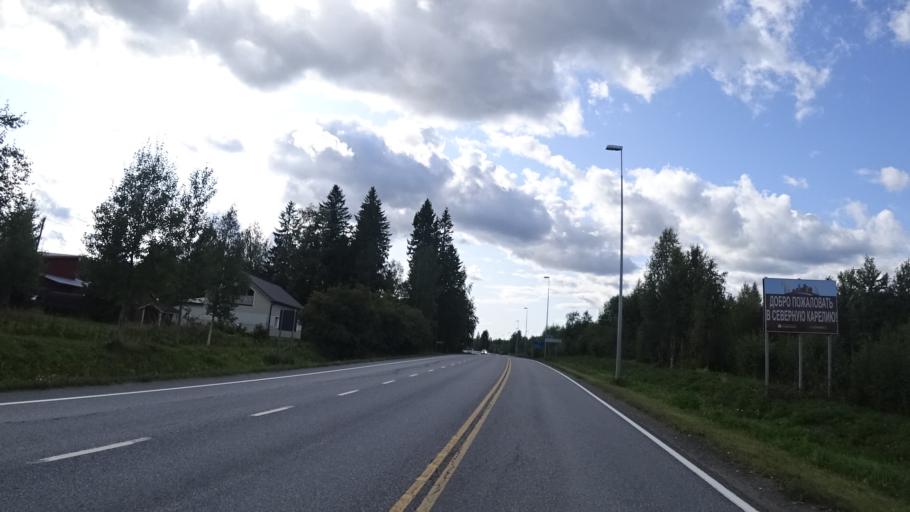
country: RU
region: Republic of Karelia
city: Vyartsilya
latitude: 62.1765
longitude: 30.5867
